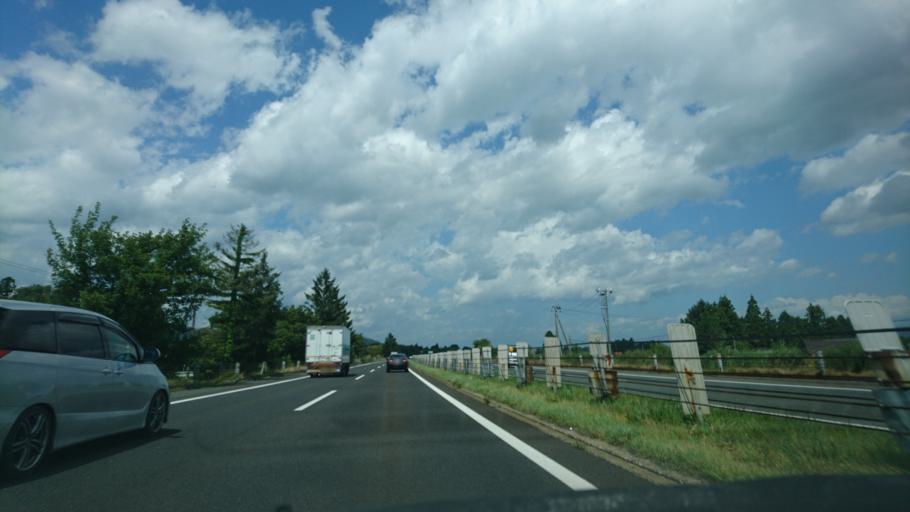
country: JP
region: Iwate
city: Morioka-shi
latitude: 39.5831
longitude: 141.1186
